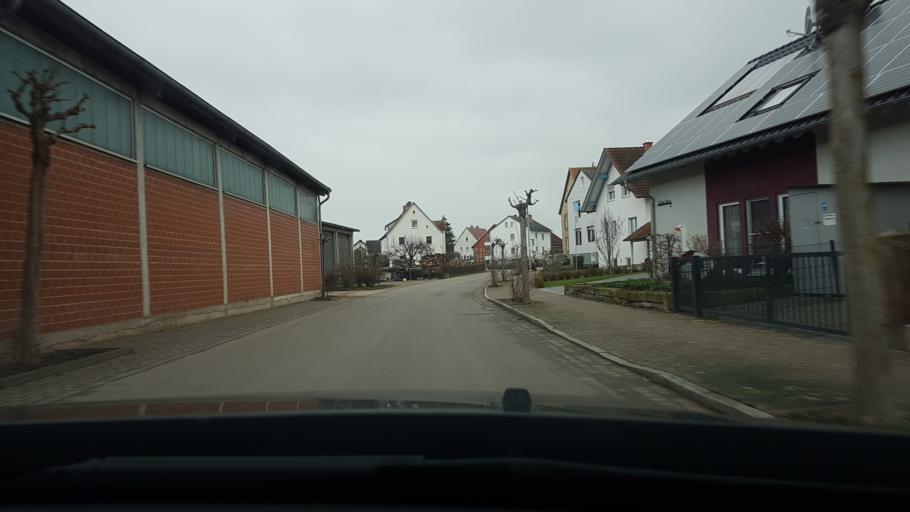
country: DE
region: Hesse
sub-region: Regierungsbezirk Kassel
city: Volkmarsen
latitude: 51.4160
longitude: 9.1113
